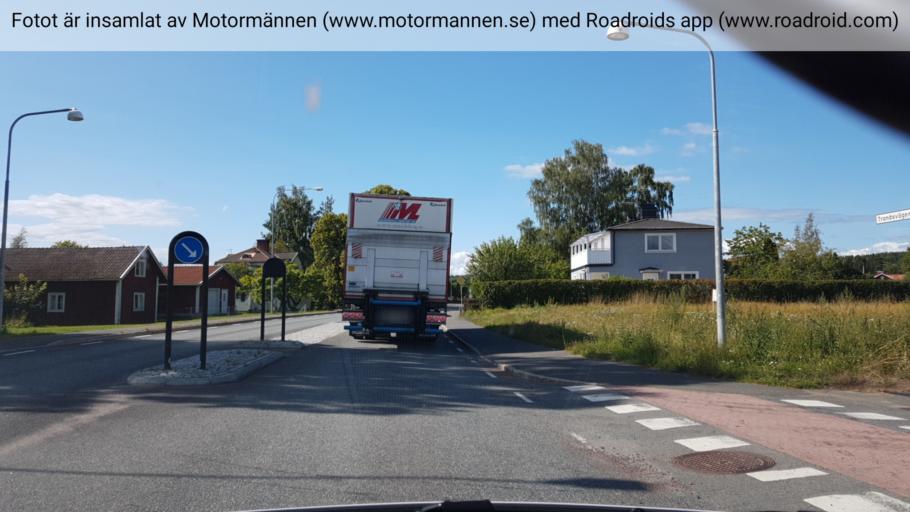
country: SE
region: Joenkoeping
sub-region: Jonkopings Kommun
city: Asa
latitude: 58.0073
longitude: 14.5759
